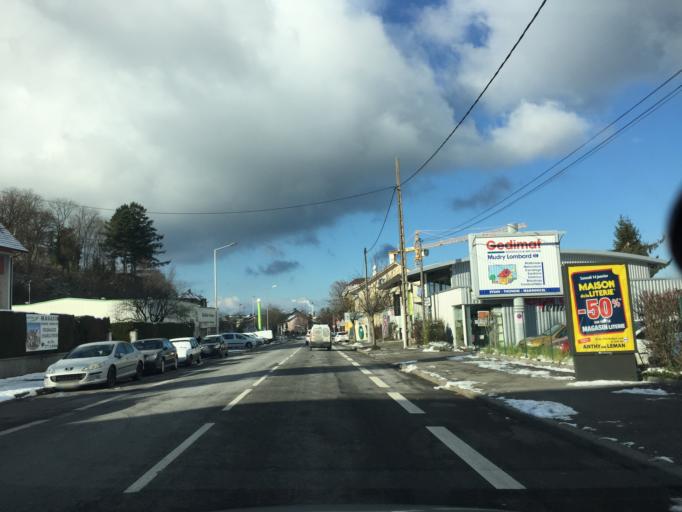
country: FR
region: Rhone-Alpes
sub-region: Departement de la Haute-Savoie
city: Thonon-les-Bains
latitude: 46.3703
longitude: 6.4930
